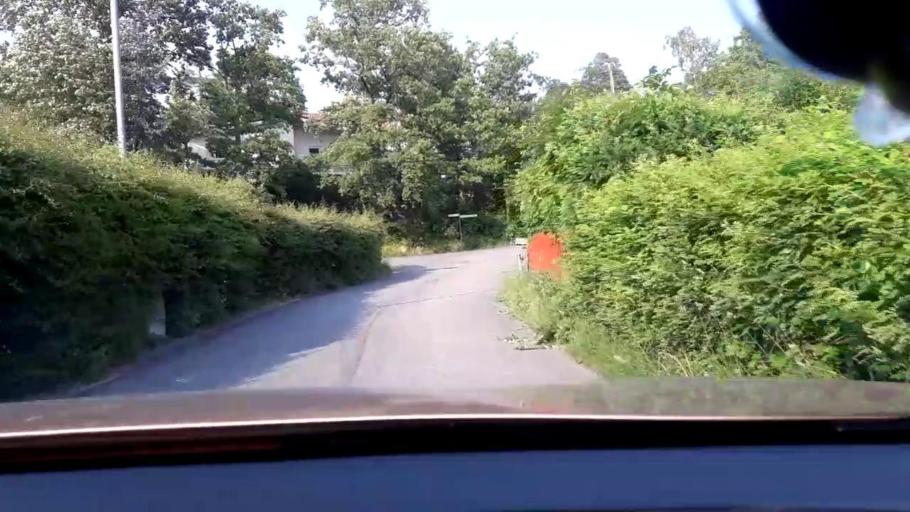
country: SE
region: Stockholm
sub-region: Lidingo
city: Brevik
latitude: 59.3217
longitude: 18.2075
